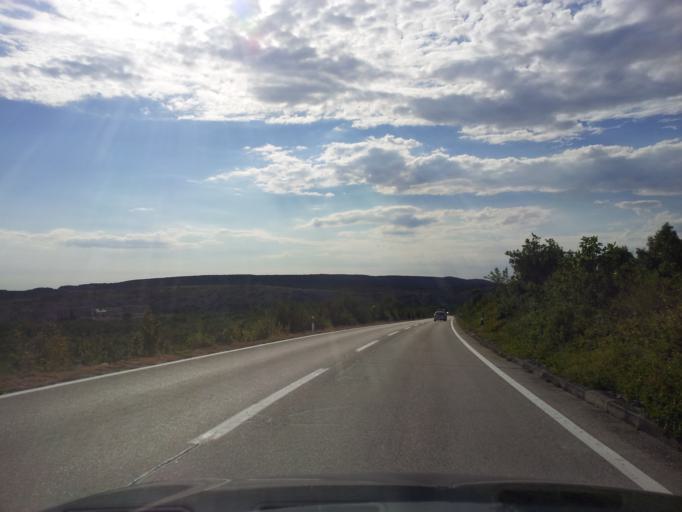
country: HR
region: Zadarska
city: Posedarje
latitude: 44.2284
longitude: 15.5384
